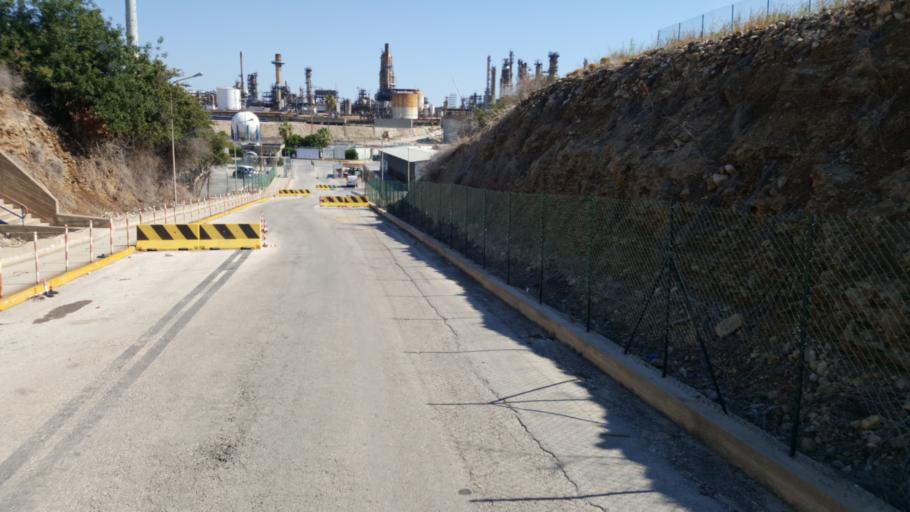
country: IT
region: Sicily
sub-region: Provincia di Siracusa
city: Melilli
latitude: 37.2063
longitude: 15.1664
